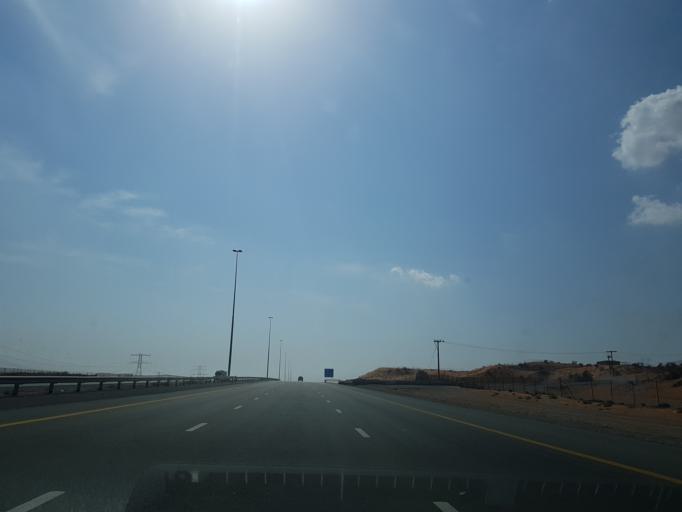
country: AE
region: Ra's al Khaymah
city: Ras al-Khaimah
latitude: 25.6850
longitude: 55.9118
